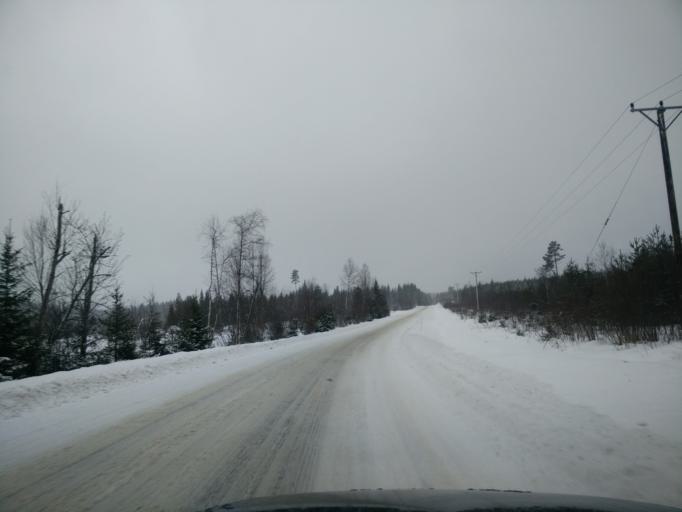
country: SE
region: Vaesternorrland
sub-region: Ange Kommun
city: Ange
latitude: 62.4667
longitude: 15.4536
